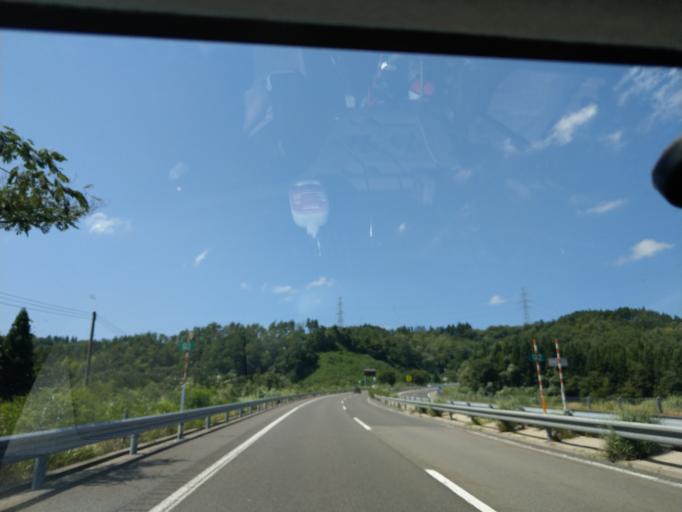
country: JP
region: Akita
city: Omagari
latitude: 39.5708
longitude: 140.3014
